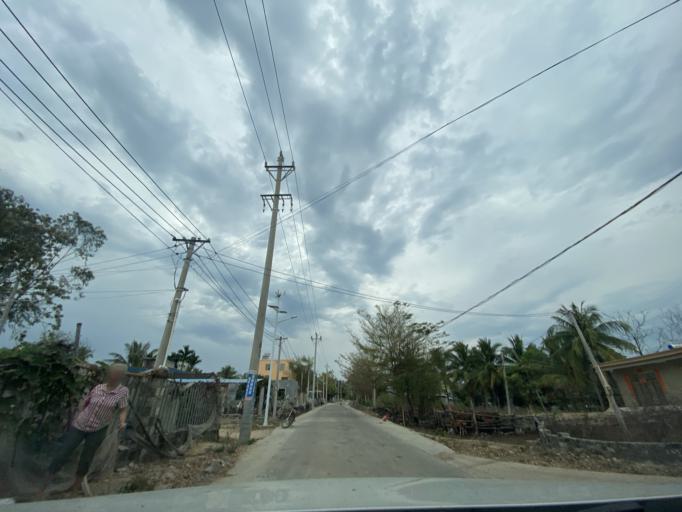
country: CN
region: Hainan
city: Yingzhou
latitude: 18.4177
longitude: 109.8230
